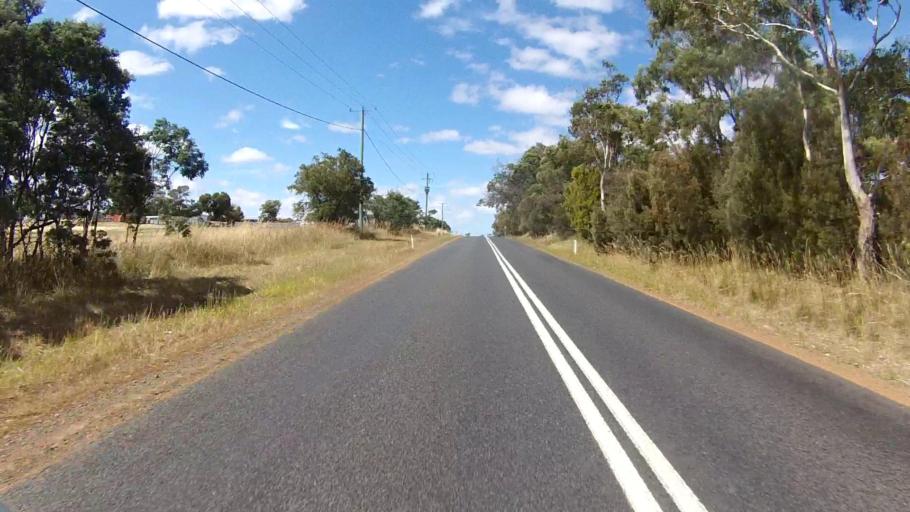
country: AU
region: Tasmania
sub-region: Sorell
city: Sorell
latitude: -42.6161
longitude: 147.4287
